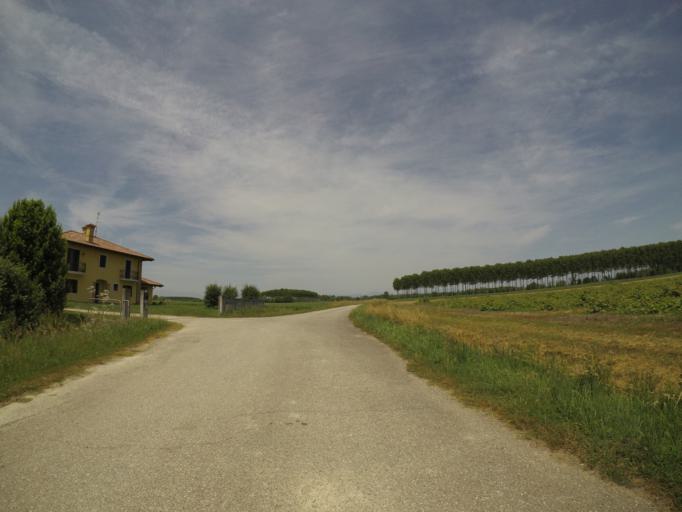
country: IT
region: Friuli Venezia Giulia
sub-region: Provincia di Udine
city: Camino al Tagliamento
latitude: 45.9063
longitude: 12.9597
